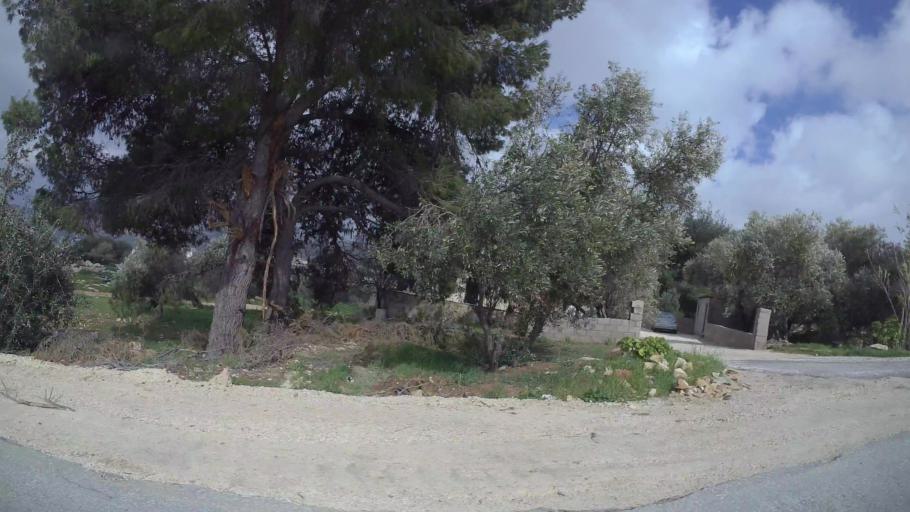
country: JO
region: Amman
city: Al Jubayhah
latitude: 32.0682
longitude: 35.8692
